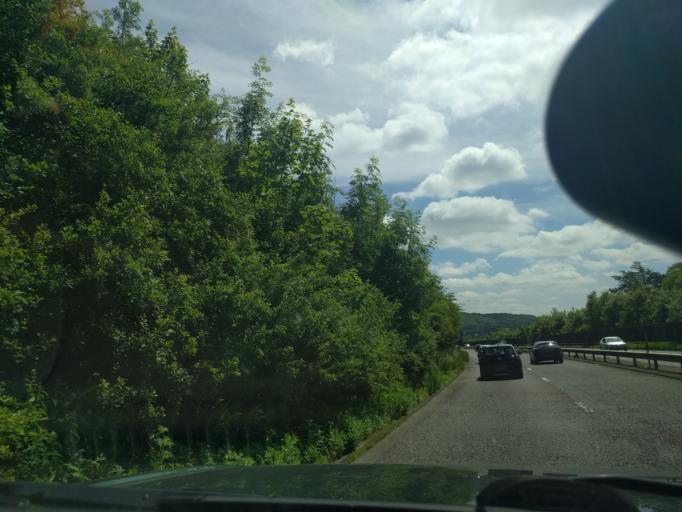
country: GB
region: England
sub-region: Bath and North East Somerset
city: Bath
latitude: 51.4103
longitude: -2.3432
